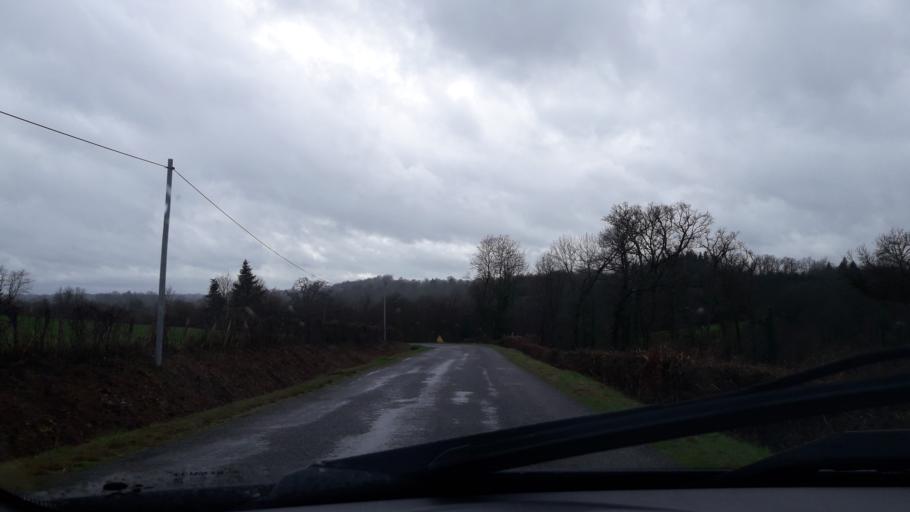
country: FR
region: Limousin
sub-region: Departement de la Haute-Vienne
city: Saint-Paul
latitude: 45.7698
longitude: 1.4315
